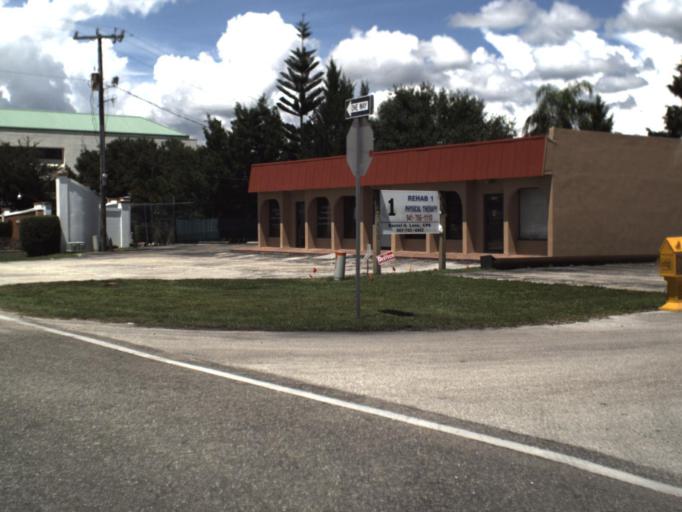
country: US
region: Florida
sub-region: Charlotte County
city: Port Charlotte
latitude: 26.9694
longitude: -82.0810
